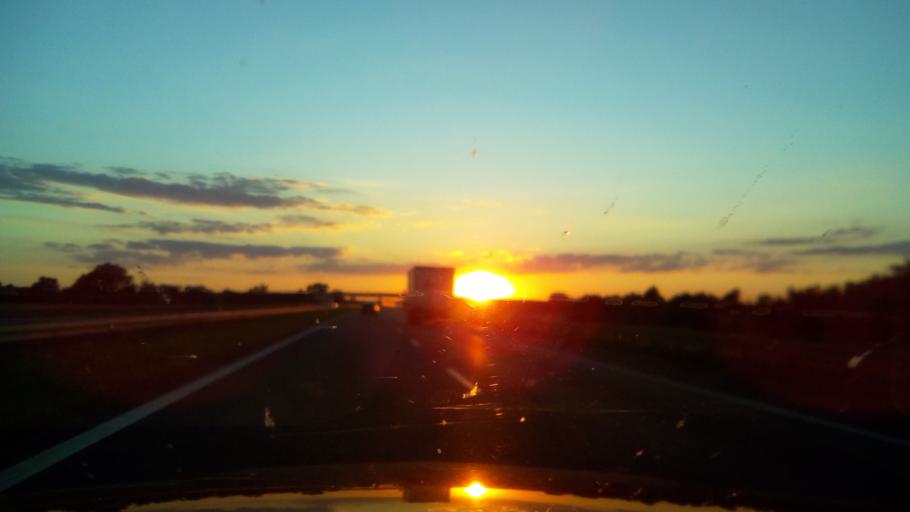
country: PL
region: Lodz Voivodeship
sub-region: Powiat poddebicki
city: Dalikow
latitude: 51.9578
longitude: 19.1308
